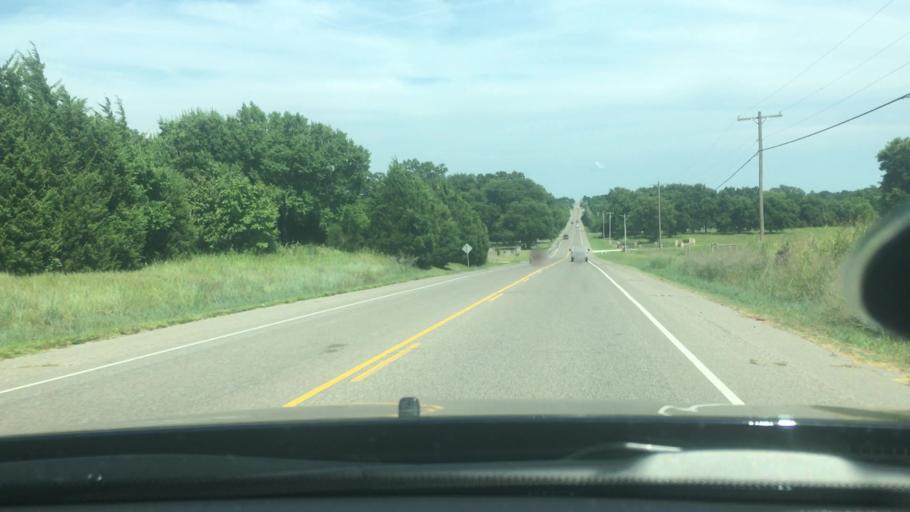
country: US
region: Oklahoma
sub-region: Pottawatomie County
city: Shawnee
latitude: 35.3331
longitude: -96.8203
